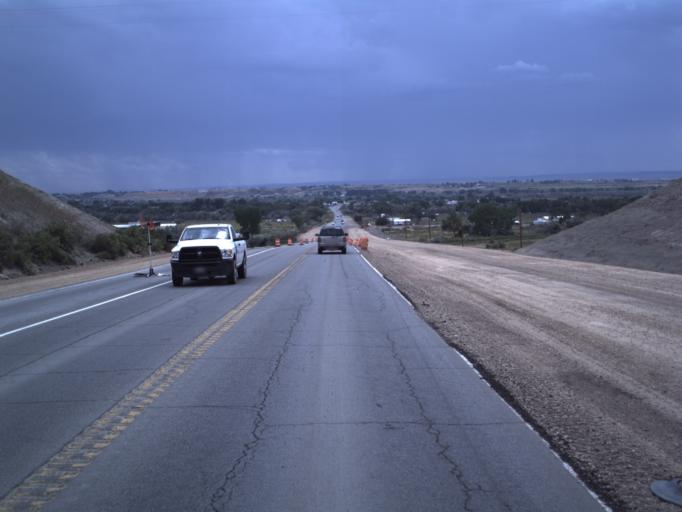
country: US
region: Utah
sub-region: Duchesne County
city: Roosevelt
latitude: 40.2178
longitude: -110.0674
